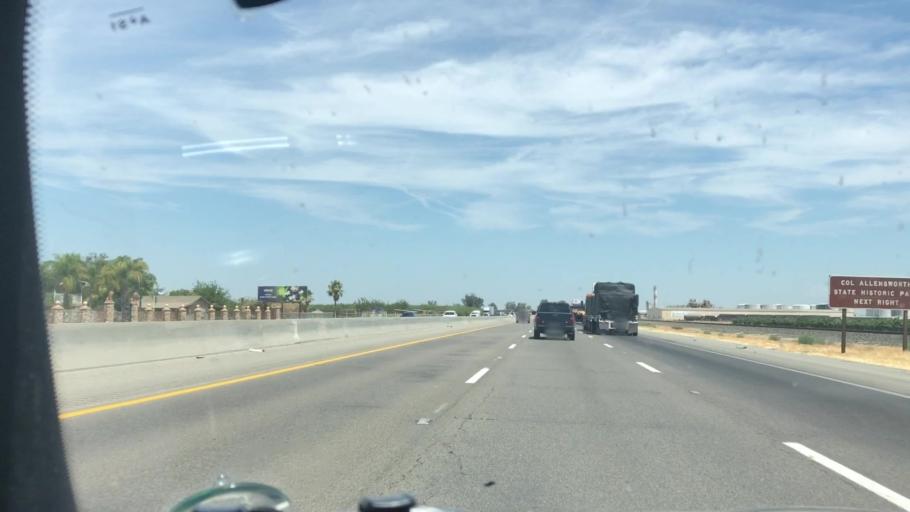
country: US
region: California
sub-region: Kern County
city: McFarland
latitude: 35.7075
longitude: -119.2340
